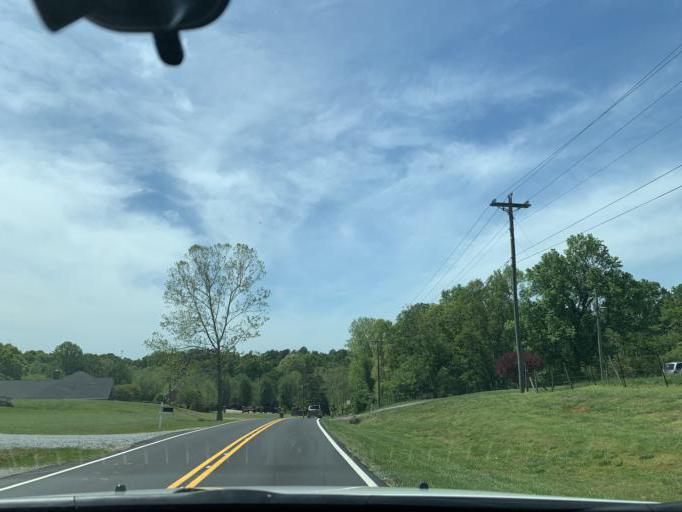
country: US
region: Georgia
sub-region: Forsyth County
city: Cumming
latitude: 34.2643
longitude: -84.0505
